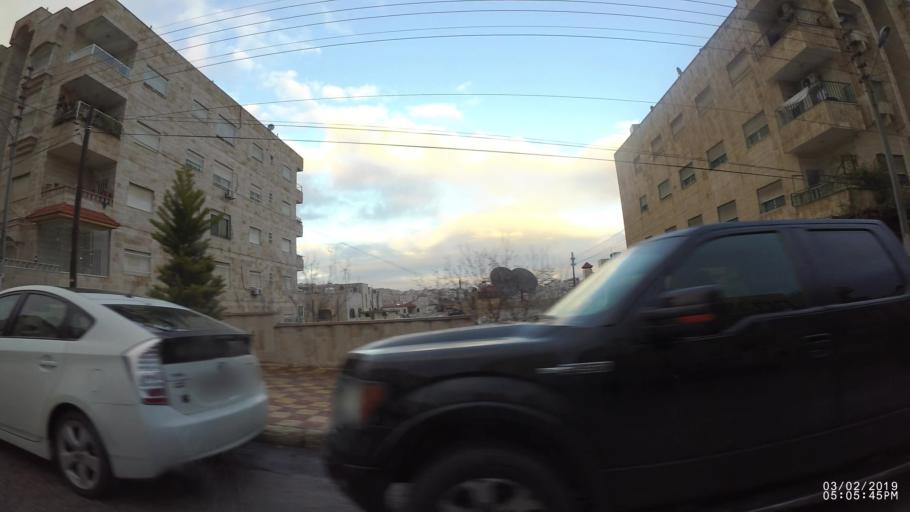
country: JO
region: Amman
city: Amman
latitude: 31.9863
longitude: 35.9158
